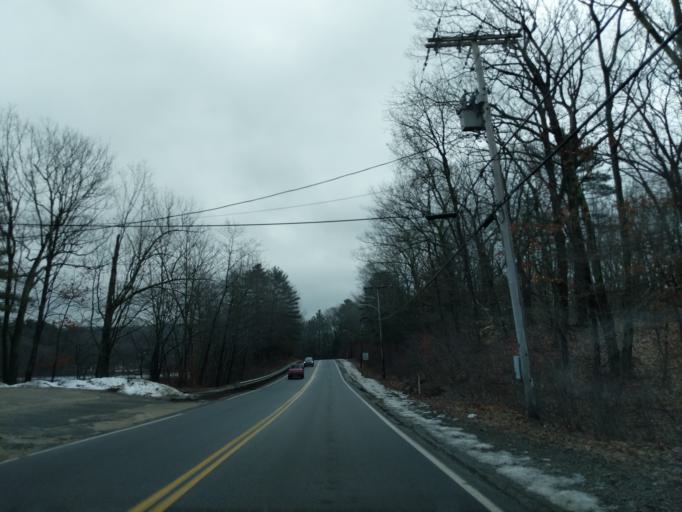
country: US
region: Massachusetts
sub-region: Worcester County
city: Webster
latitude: 42.0607
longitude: -71.8538
